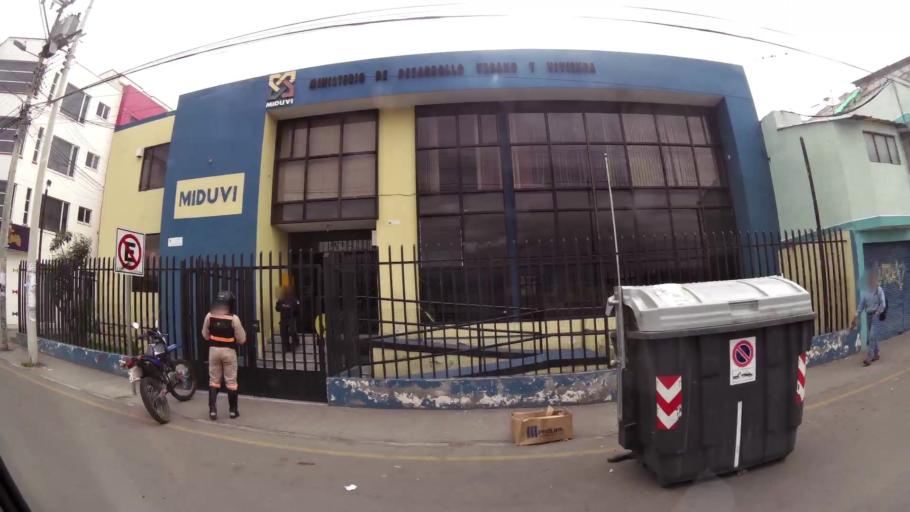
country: EC
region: Cotopaxi
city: Latacunga
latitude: -0.9349
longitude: -78.6215
